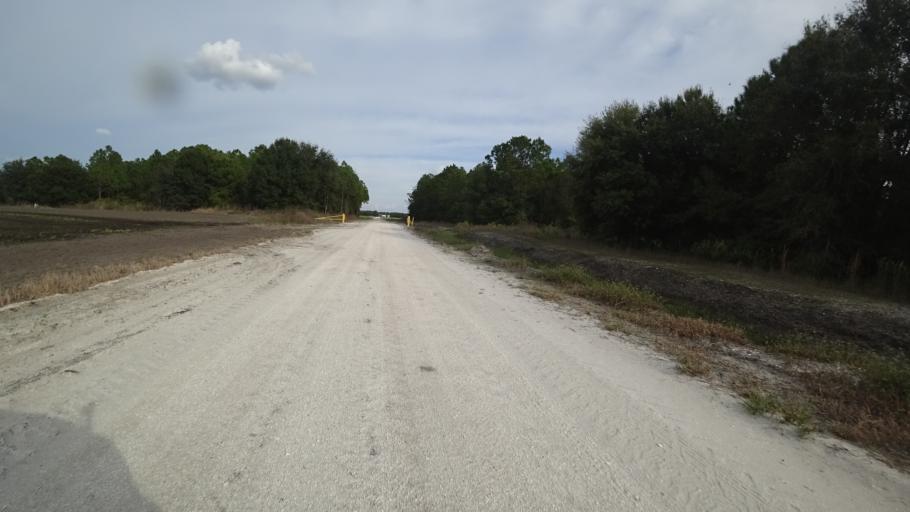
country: US
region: Florida
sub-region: Hillsborough County
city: Wimauma
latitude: 27.5620
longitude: -82.1004
